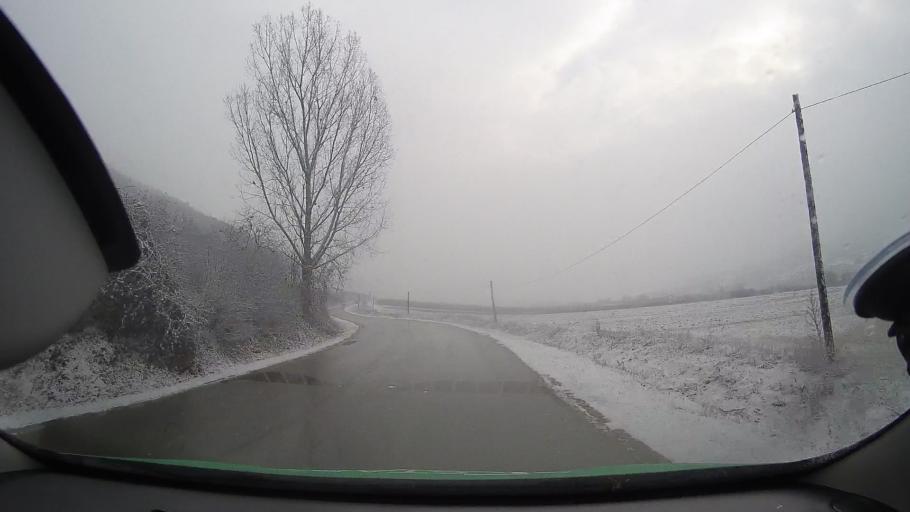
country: RO
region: Alba
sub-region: Comuna Lopadea Noua
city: Lopadea Noua
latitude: 46.3041
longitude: 23.8011
